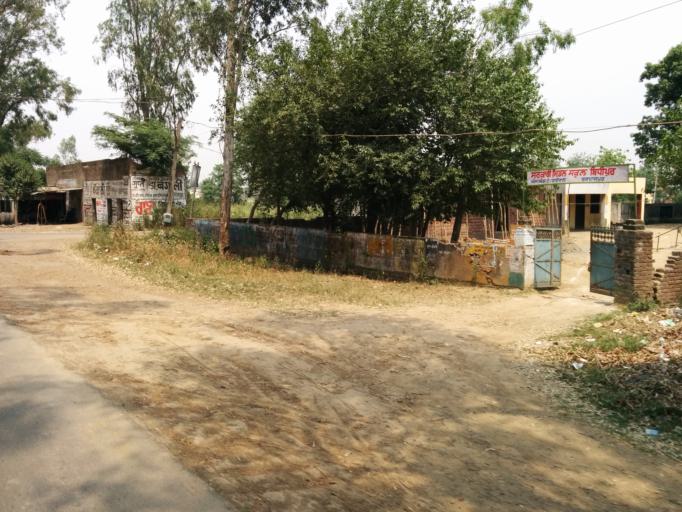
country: IN
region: Punjab
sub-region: Gurdaspur
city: Dhariwal
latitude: 31.9329
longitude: 75.3059
